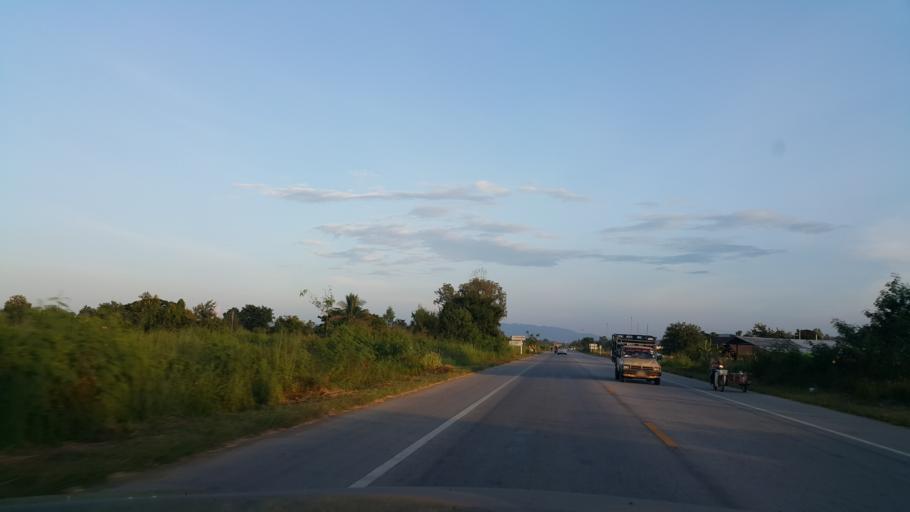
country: TH
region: Lamphun
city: Pa Sang
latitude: 18.5003
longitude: 98.8863
